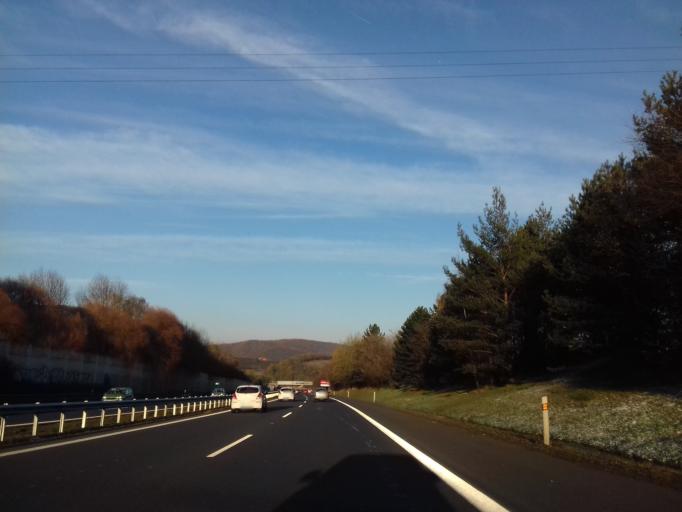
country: CZ
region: Central Bohemia
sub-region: Okres Beroun
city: Lodenice
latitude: 49.9833
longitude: 14.1355
